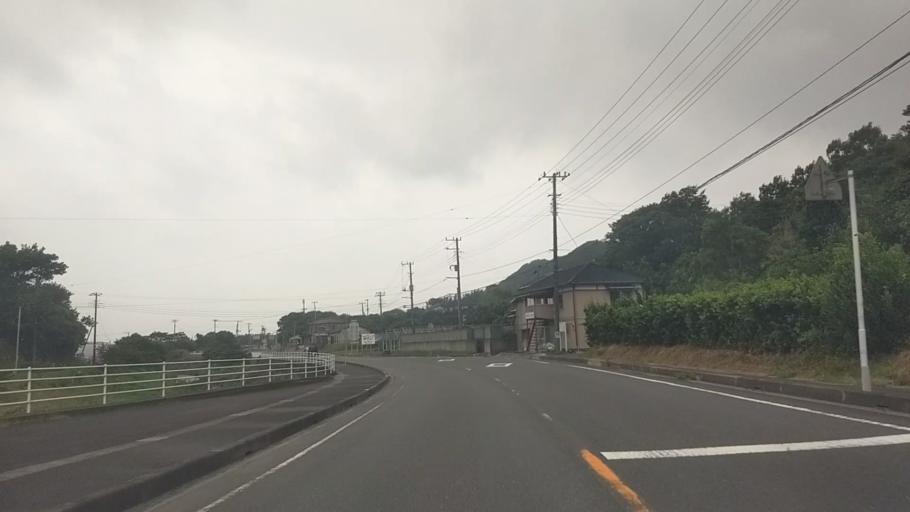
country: JP
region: Chiba
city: Tateyama
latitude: 35.1447
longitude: 139.8546
